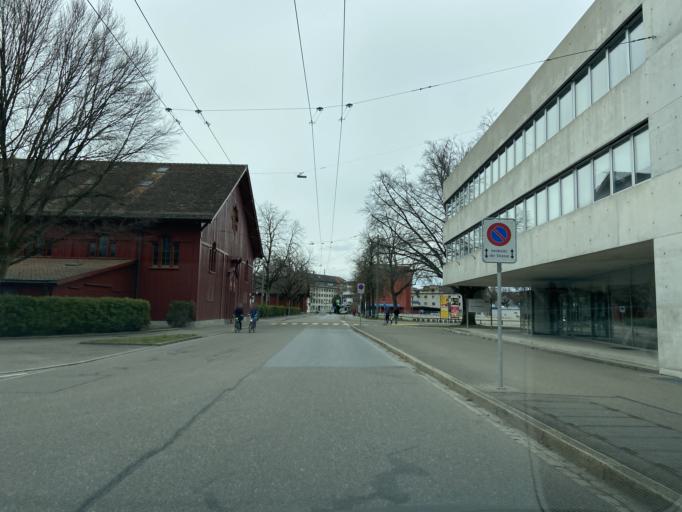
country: CH
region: Zurich
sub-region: Bezirk Winterthur
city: Mattenbach (Kreis 7) / Deutweg
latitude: 47.4950
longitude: 8.7332
